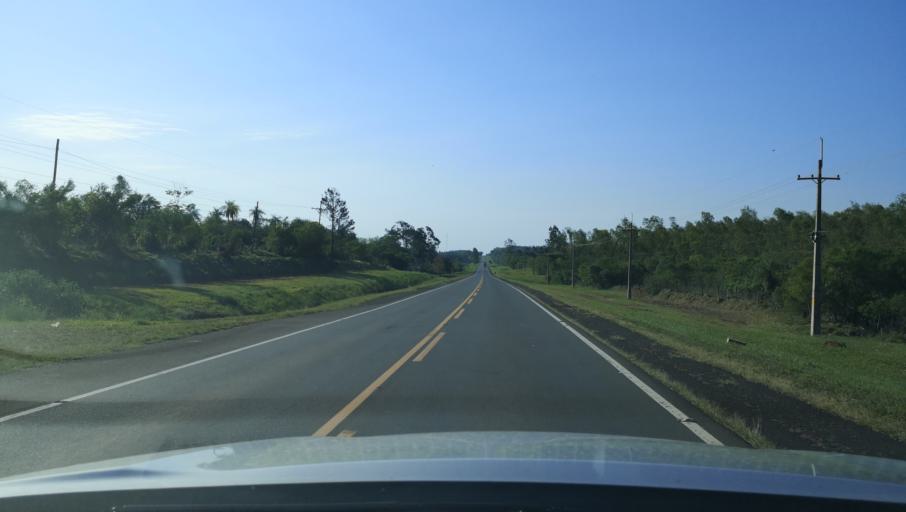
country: PY
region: Misiones
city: Santa Maria
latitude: -26.7573
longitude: -57.0356
